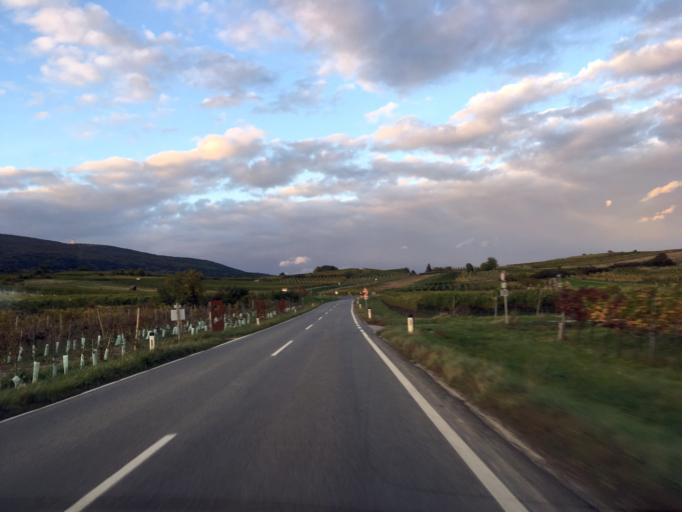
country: AT
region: Lower Austria
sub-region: Politischer Bezirk Baden
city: Pfaffstatten
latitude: 48.0227
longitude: 16.2583
